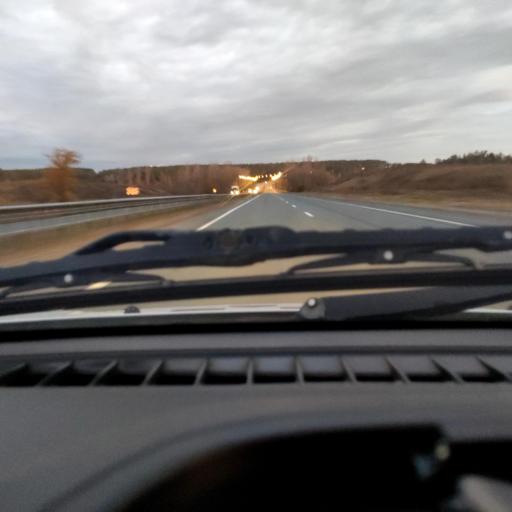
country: RU
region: Samara
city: Zhigulevsk
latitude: 53.5257
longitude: 49.5255
